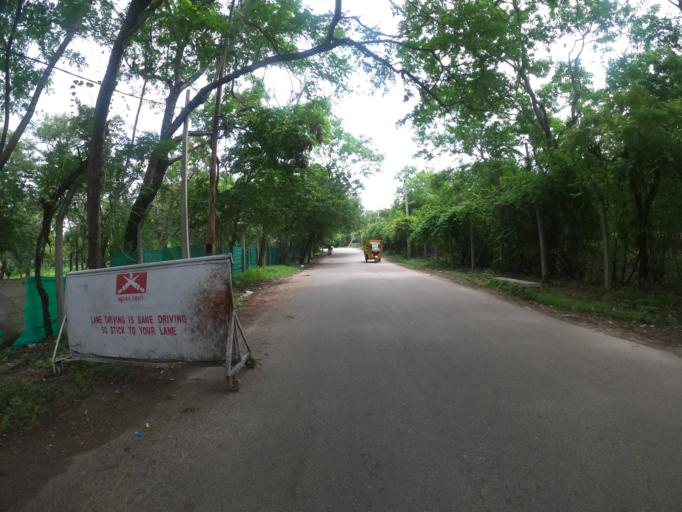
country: IN
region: Telangana
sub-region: Hyderabad
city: Hyderabad
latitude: 17.3918
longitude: 78.4198
